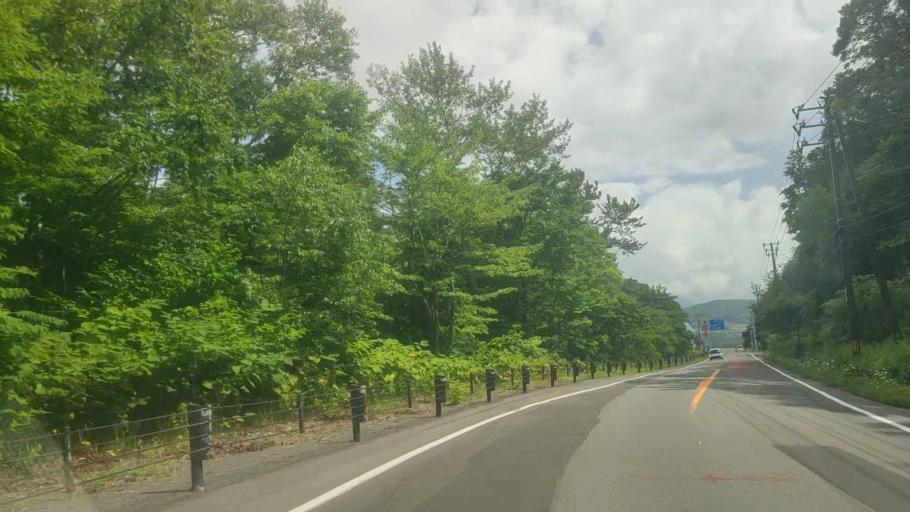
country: JP
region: Hokkaido
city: Date
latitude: 42.5643
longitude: 140.8833
